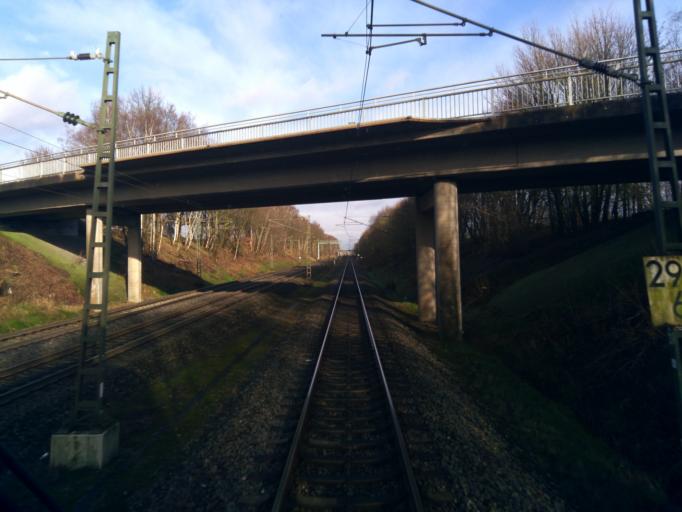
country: DE
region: Lower Saxony
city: Scheessel
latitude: 53.1569
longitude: 9.4850
